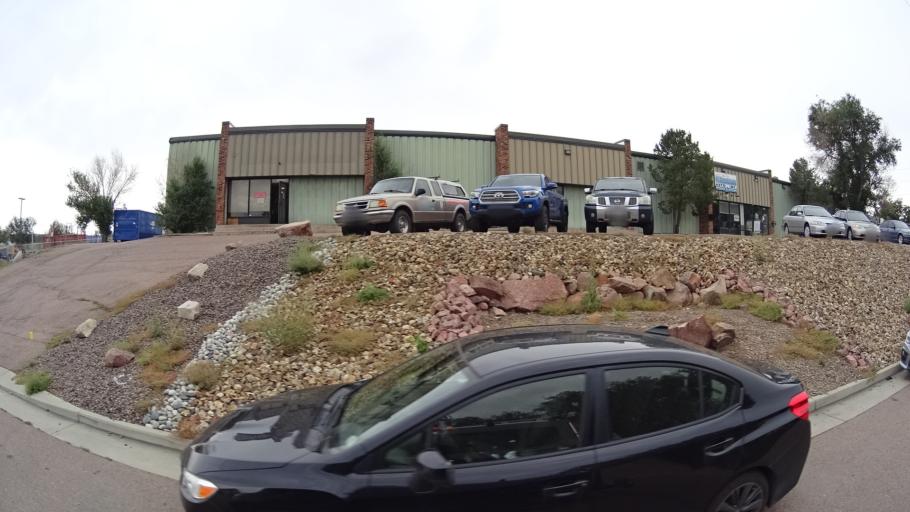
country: US
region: Colorado
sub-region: El Paso County
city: Air Force Academy
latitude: 38.9267
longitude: -104.8109
